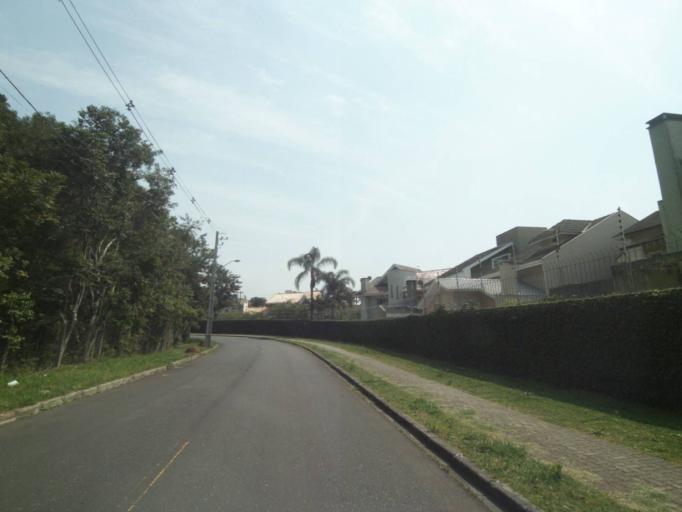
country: BR
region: Parana
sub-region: Sao Jose Dos Pinhais
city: Sao Jose dos Pinhais
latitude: -25.4876
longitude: -49.2091
